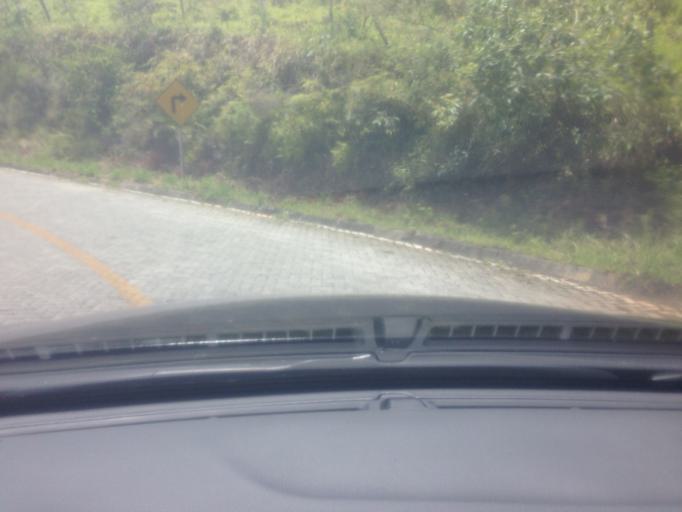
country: BR
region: Espirito Santo
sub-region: Guarapari
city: Guarapari
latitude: -20.6045
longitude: -40.5361
